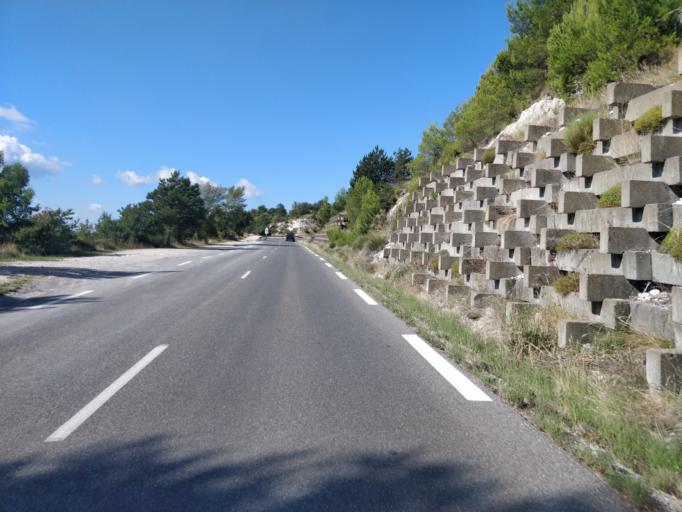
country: FR
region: Provence-Alpes-Cote d'Azur
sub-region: Departement des Alpes-de-Haute-Provence
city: Riez
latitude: 43.8041
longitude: 6.2367
